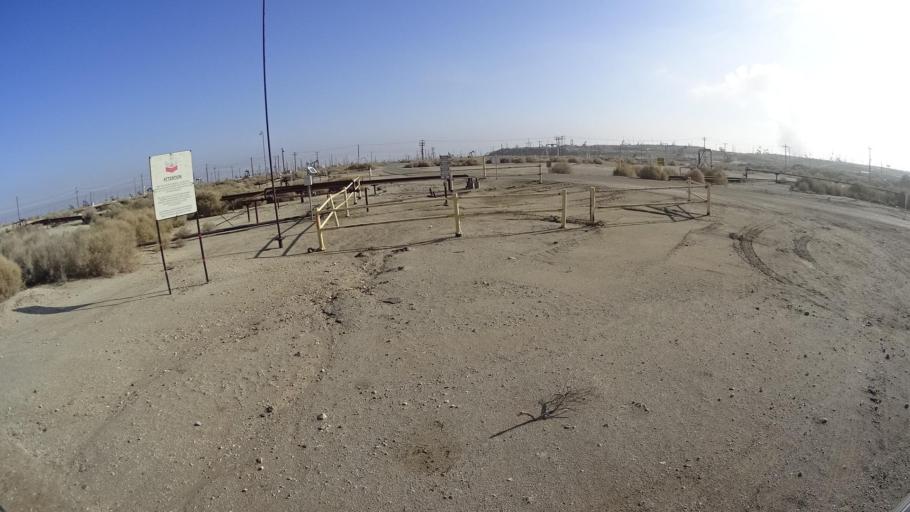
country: US
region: California
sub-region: Kern County
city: Taft Heights
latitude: 35.2224
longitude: -119.5972
